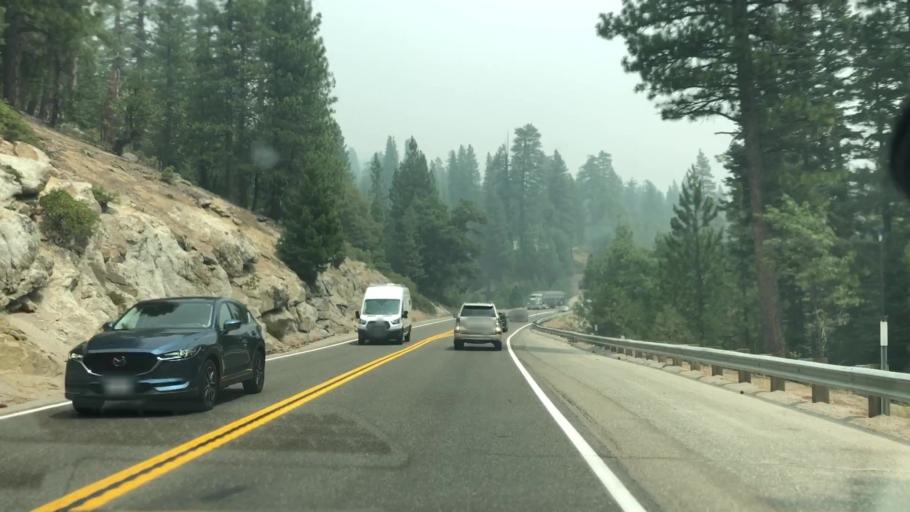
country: US
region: California
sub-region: El Dorado County
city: South Lake Tahoe
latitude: 38.7842
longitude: -120.2151
